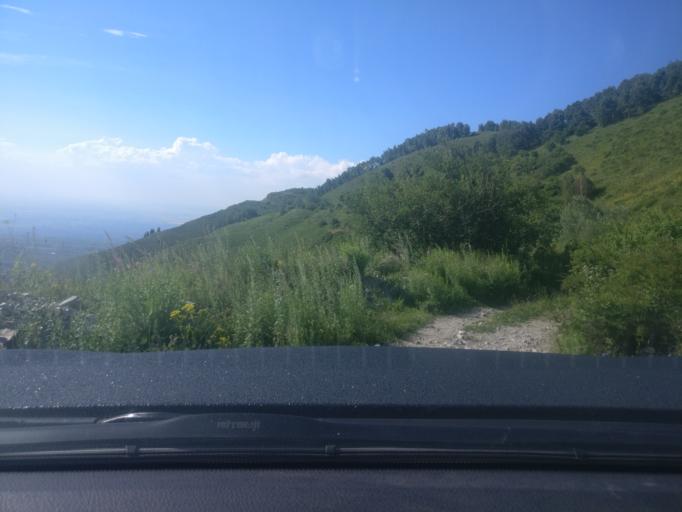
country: KZ
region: Almaty Qalasy
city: Almaty
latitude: 43.1089
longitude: 76.9327
